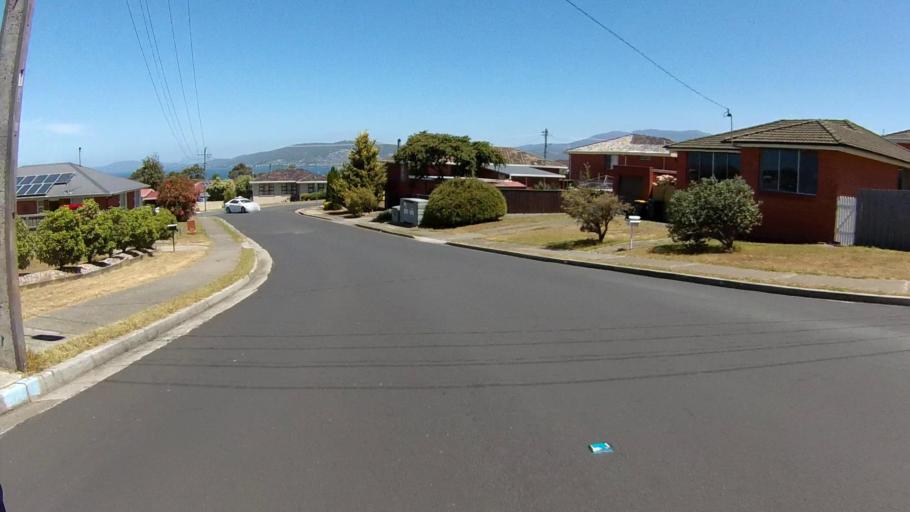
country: AU
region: Tasmania
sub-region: Clarence
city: Howrah
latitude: -42.8767
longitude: 147.4096
